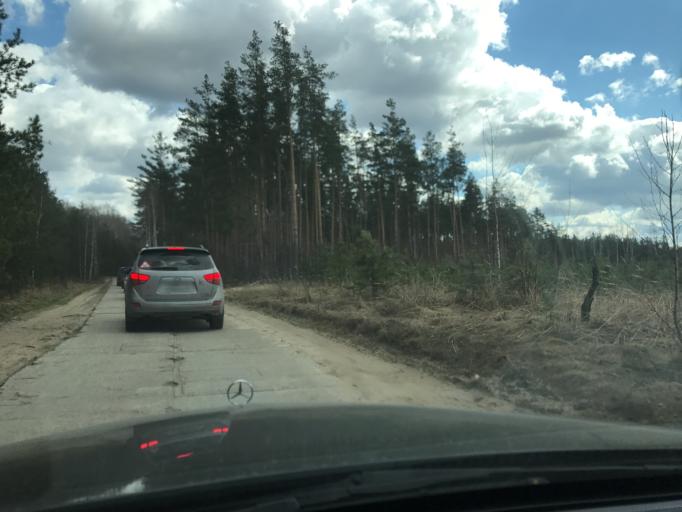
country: RU
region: Vladimir
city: Pokrov
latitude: 55.8464
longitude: 39.1595
